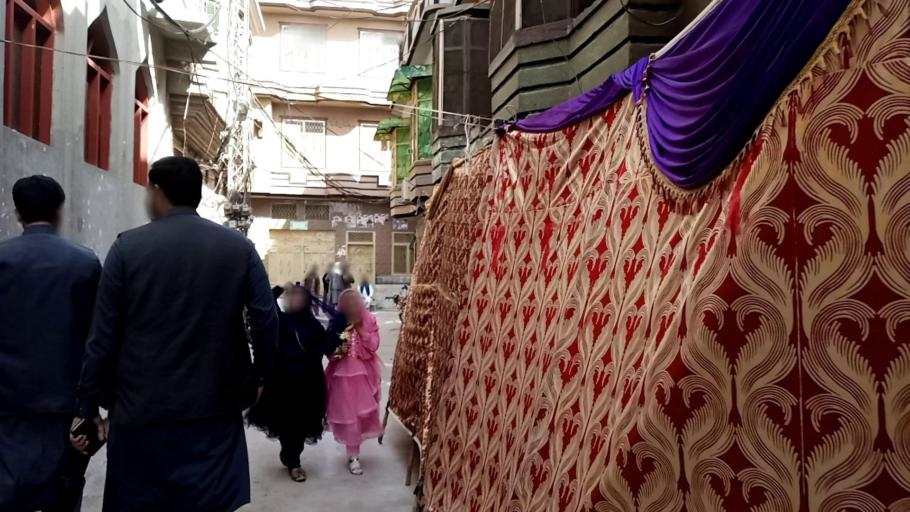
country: PK
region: Khyber Pakhtunkhwa
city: Peshawar
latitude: 34.0005
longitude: 71.5992
